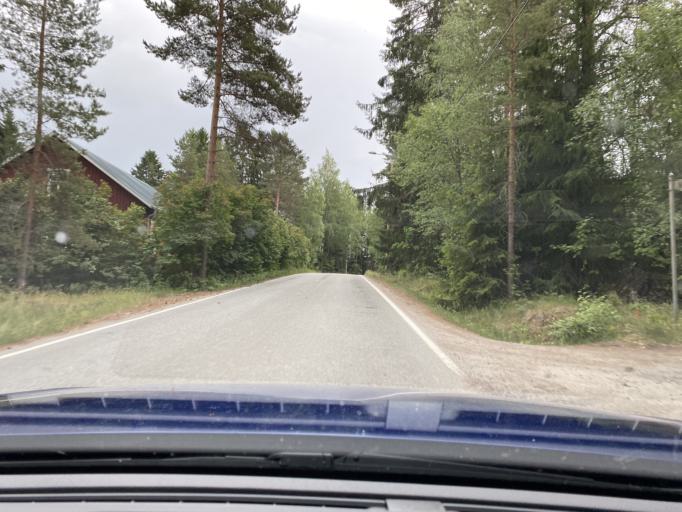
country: FI
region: Satakunta
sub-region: Rauma
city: Eura
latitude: 61.1533
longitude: 22.1191
